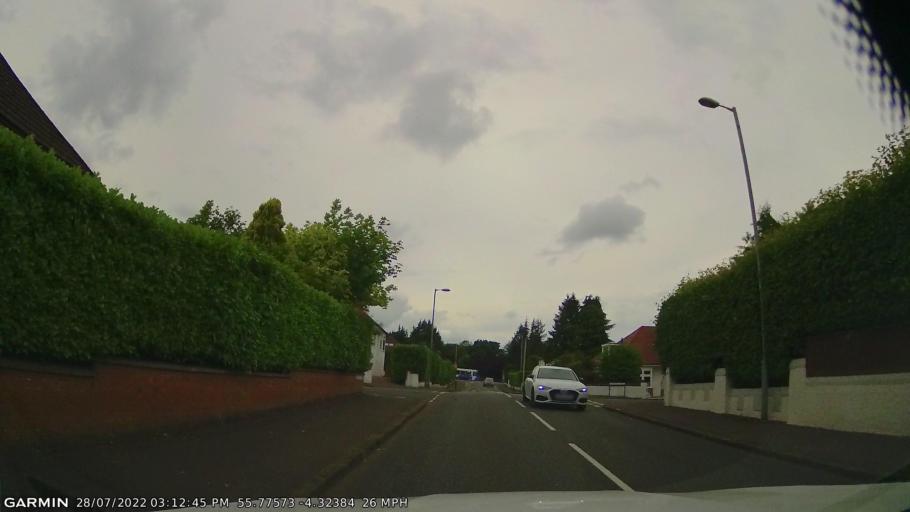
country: GB
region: Scotland
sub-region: East Renfrewshire
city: Newton Mearns
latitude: 55.7758
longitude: -4.3238
